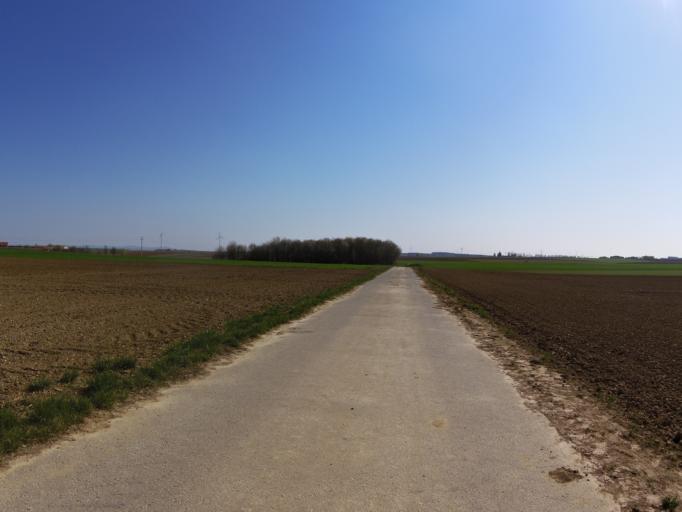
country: DE
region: Bavaria
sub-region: Regierungsbezirk Unterfranken
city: Biebelried
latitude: 49.8112
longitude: 10.0997
